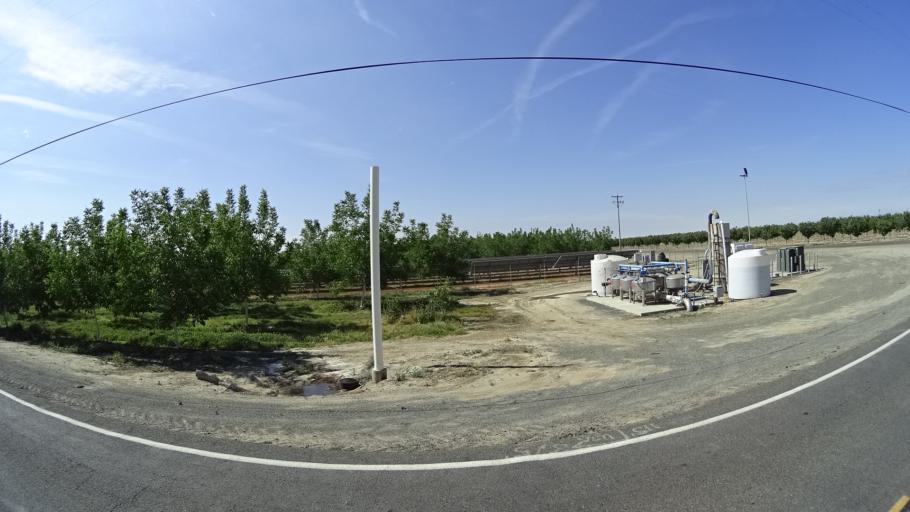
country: US
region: California
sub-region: Kings County
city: Armona
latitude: 36.2547
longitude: -119.7262
